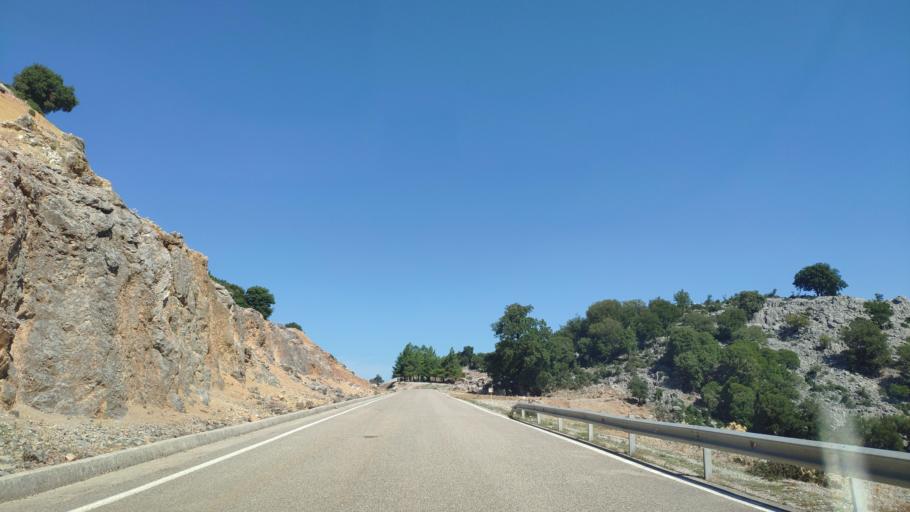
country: GR
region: Central Greece
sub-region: Nomos Evrytanias
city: Kerasochori
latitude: 38.9570
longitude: 21.4660
